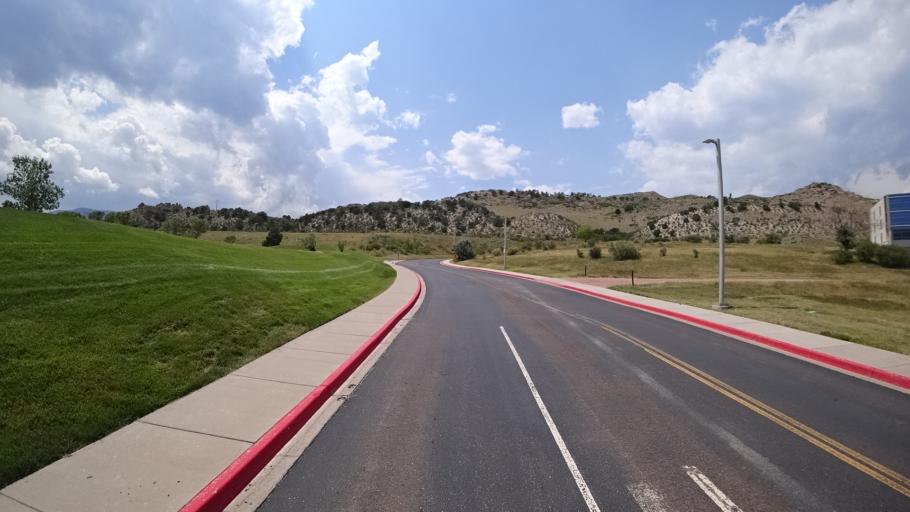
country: US
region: Colorado
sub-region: El Paso County
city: Manitou Springs
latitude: 38.8988
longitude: -104.8738
